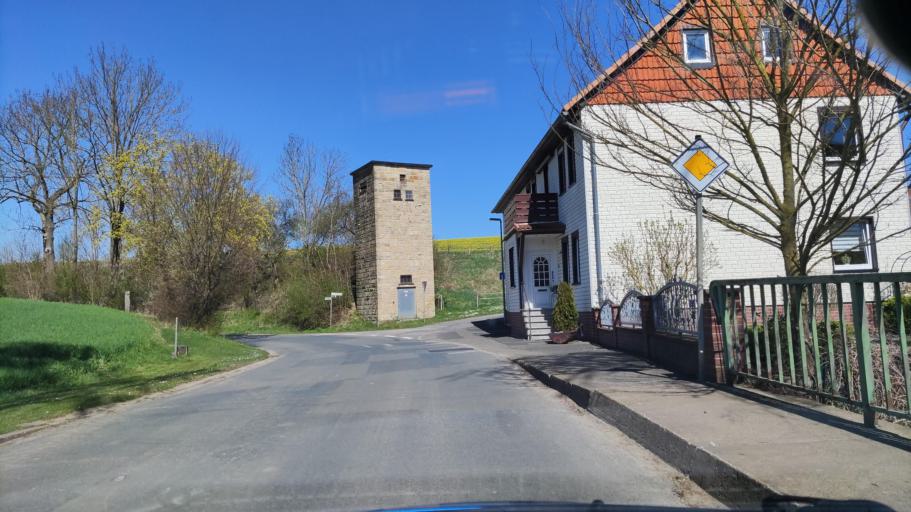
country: DE
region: Lower Saxony
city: Einbeck
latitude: 51.8662
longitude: 9.8632
